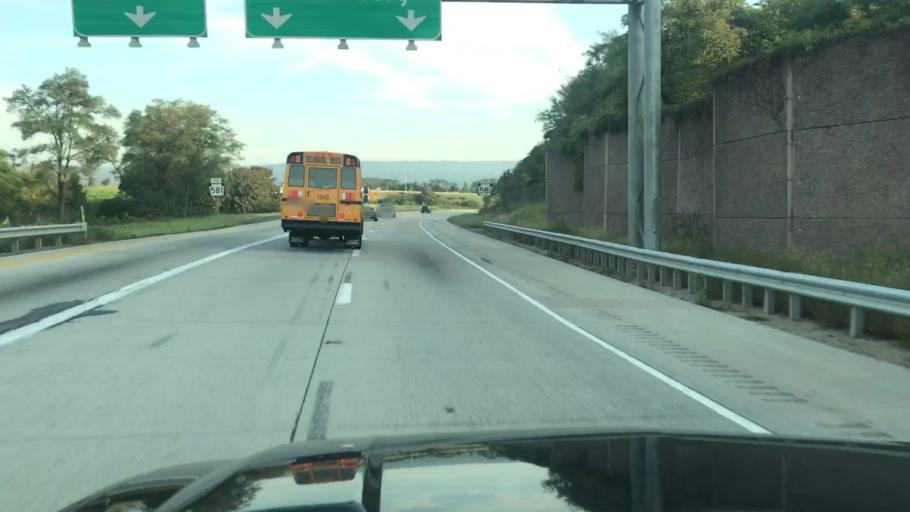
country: US
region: Pennsylvania
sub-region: Cumberland County
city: Mechanicsburg
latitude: 40.2706
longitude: -77.0000
